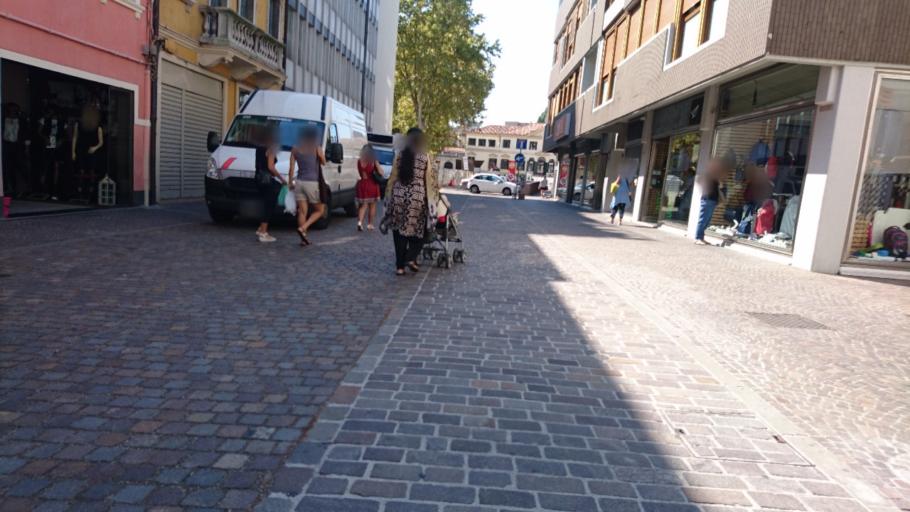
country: IT
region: Veneto
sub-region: Provincia di Venezia
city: Mestre
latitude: 45.4923
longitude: 12.2394
